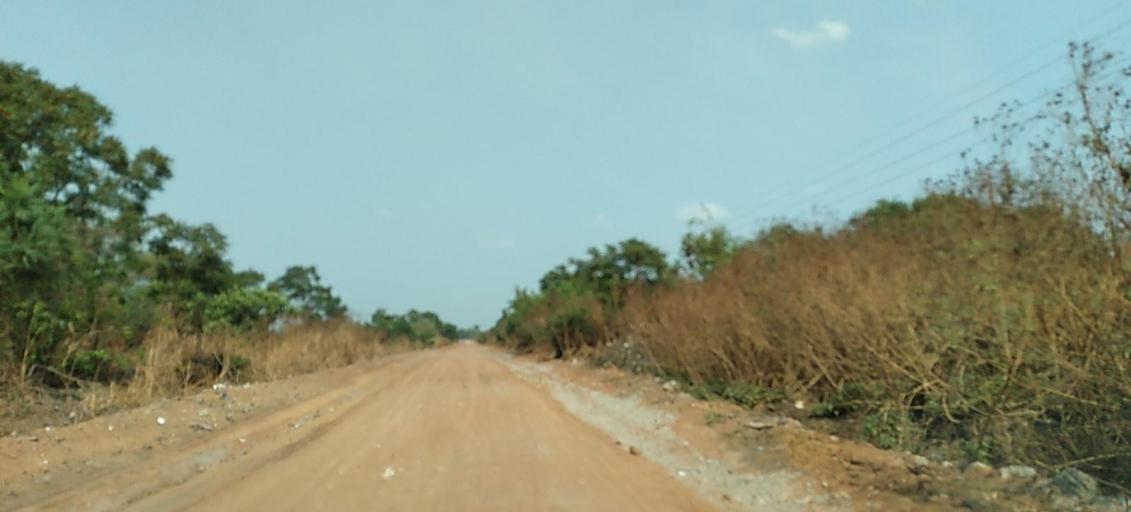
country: ZM
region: Copperbelt
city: Luanshya
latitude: -13.0946
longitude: 28.3168
